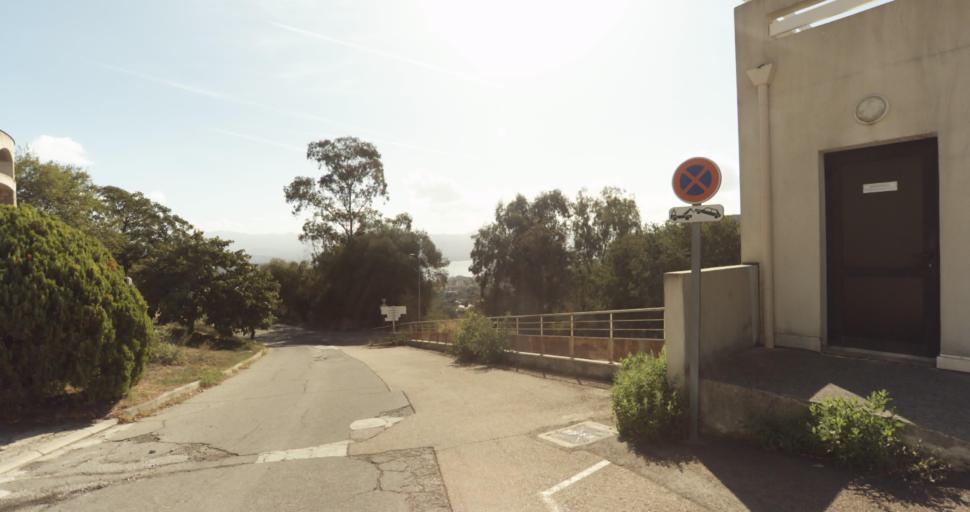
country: FR
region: Corsica
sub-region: Departement de la Corse-du-Sud
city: Ajaccio
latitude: 41.9349
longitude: 8.7154
